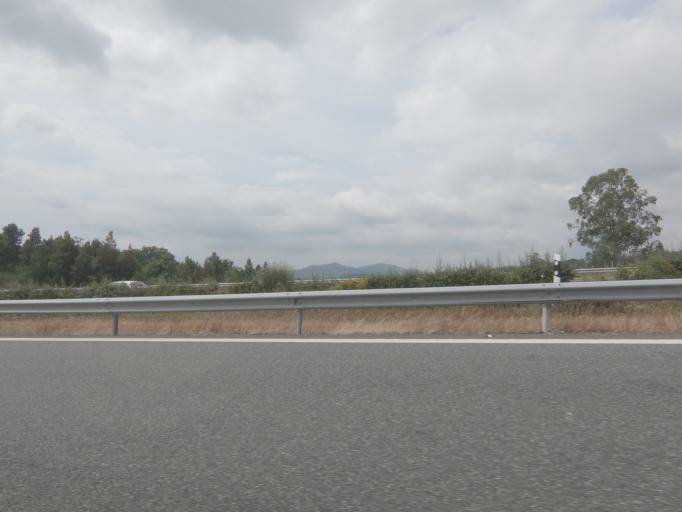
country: ES
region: Galicia
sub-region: Provincia de Pontevedra
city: Ponteareas
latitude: 42.1437
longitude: -8.4583
